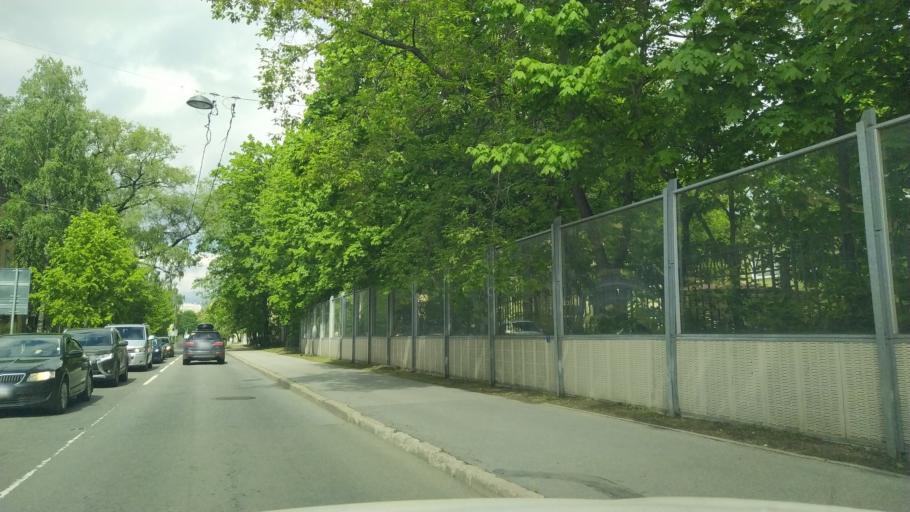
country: RU
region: St.-Petersburg
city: Novaya Derevnya
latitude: 59.9832
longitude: 30.2782
